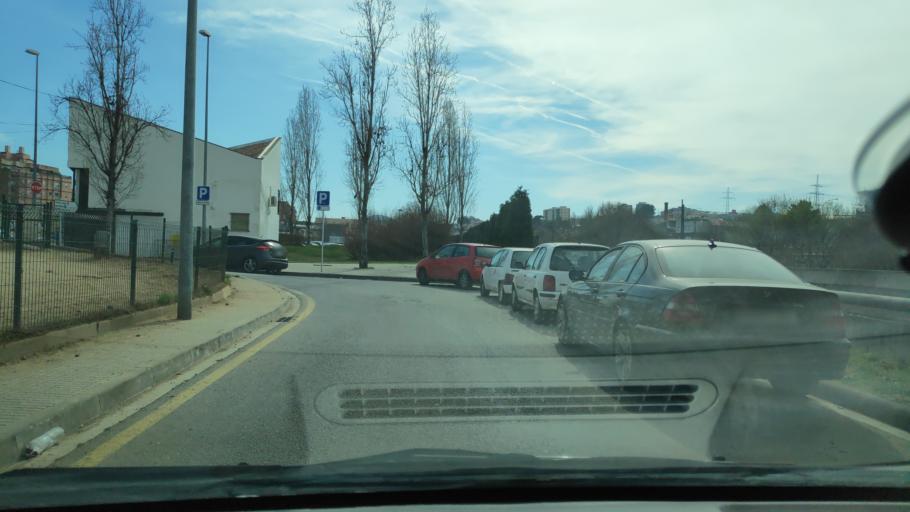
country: ES
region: Catalonia
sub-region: Provincia de Barcelona
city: Rubi
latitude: 41.4944
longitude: 2.0290
